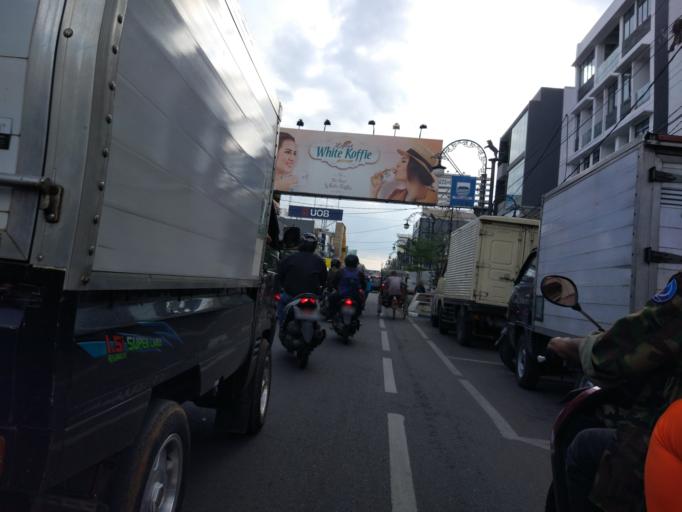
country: ID
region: West Java
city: Bandung
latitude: -6.9208
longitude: 107.6041
